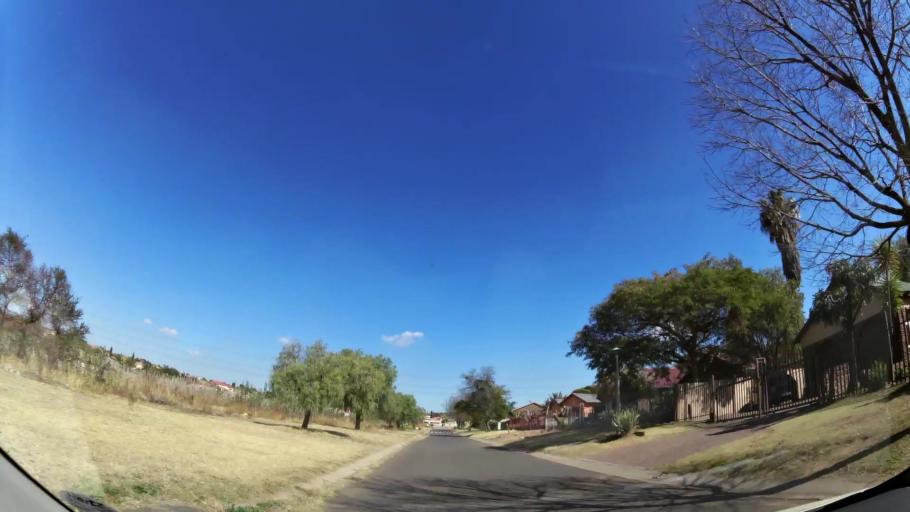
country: ZA
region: Mpumalanga
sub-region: Nkangala District Municipality
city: Witbank
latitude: -25.8577
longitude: 29.2470
